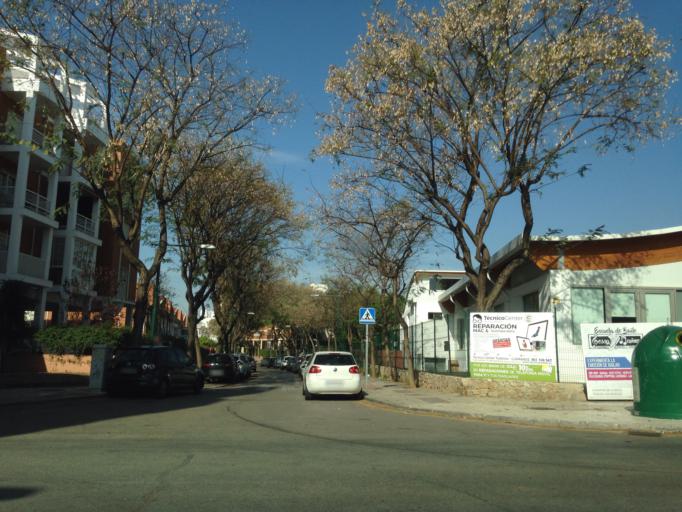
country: ES
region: Andalusia
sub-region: Provincia de Malaga
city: Malaga
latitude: 36.7224
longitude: -4.4798
